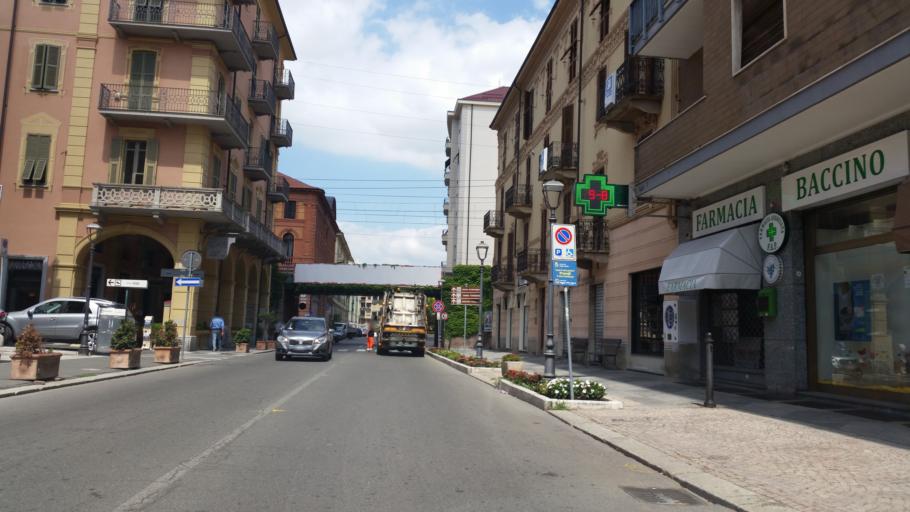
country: IT
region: Piedmont
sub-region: Provincia di Alessandria
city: Acqui Terme
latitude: 44.6717
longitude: 8.4687
